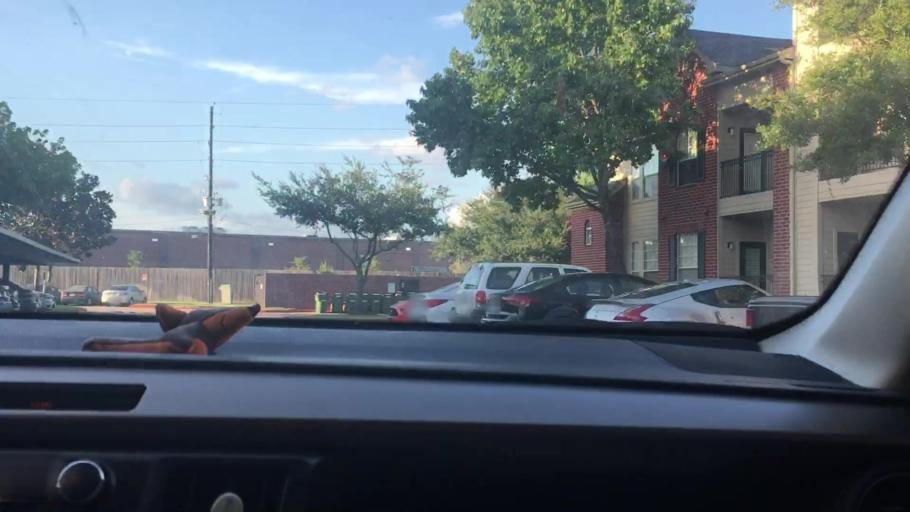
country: US
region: Texas
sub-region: Fort Bend County
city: Meadows Place
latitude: 29.6455
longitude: -95.5828
